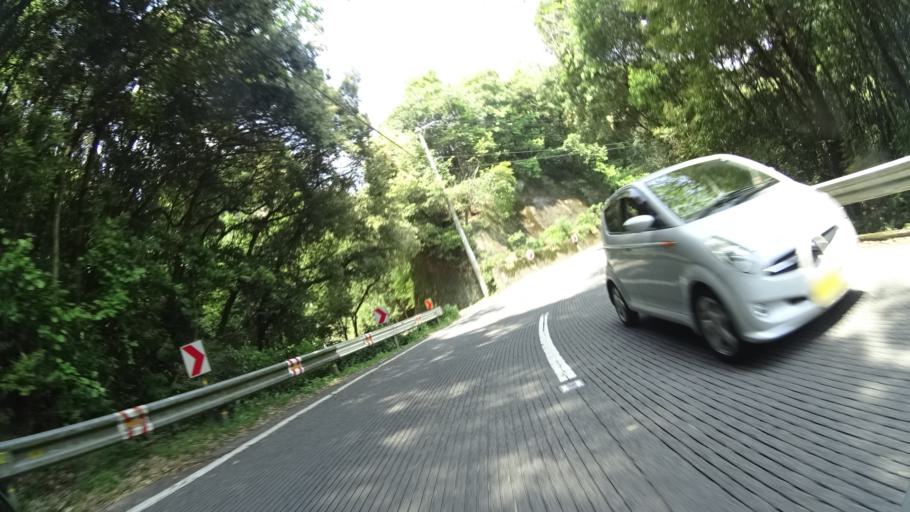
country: JP
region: Ehime
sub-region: Shikoku-chuo Shi
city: Matsuyama
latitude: 33.8727
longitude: 132.8308
